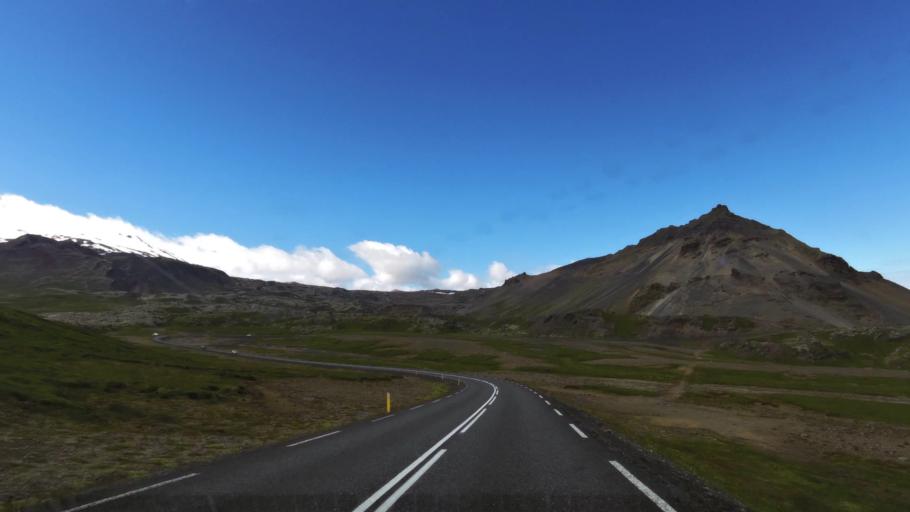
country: IS
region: West
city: Olafsvik
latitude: 64.7577
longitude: -23.6708
